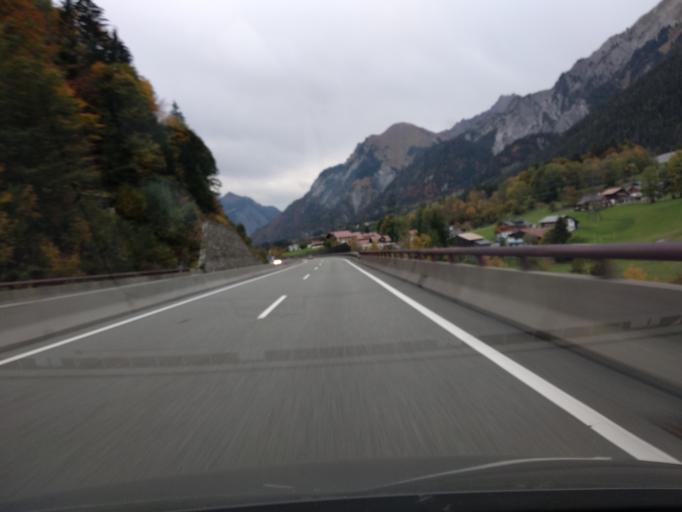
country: AT
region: Vorarlberg
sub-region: Politischer Bezirk Bludenz
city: Klosterle
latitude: 47.1302
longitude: 10.0704
